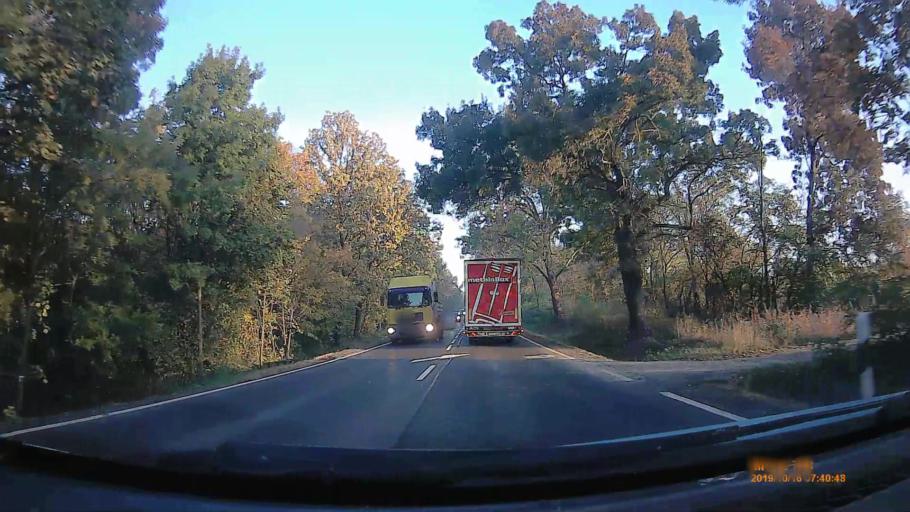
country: HU
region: Heves
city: Kerecsend
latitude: 47.8205
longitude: 20.3578
